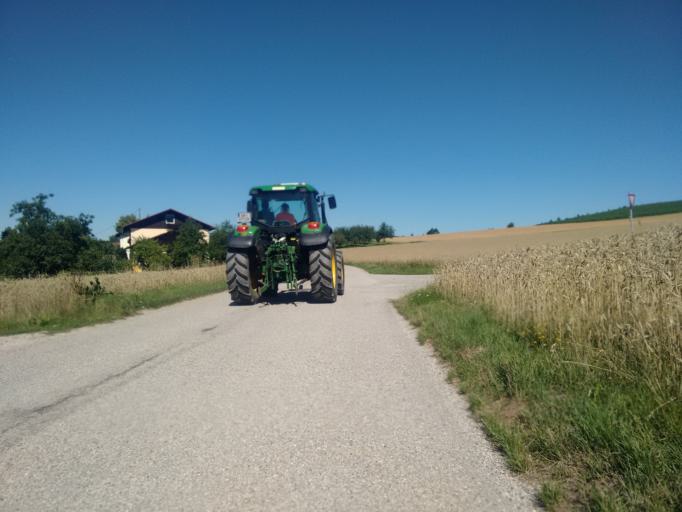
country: AT
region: Upper Austria
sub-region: Wels-Land
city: Buchkirchen
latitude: 48.2267
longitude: 13.9798
